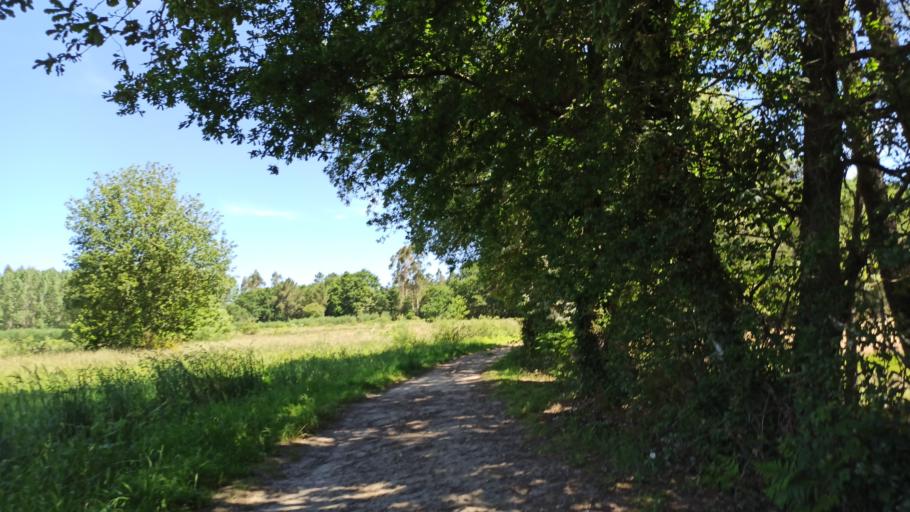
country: ES
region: Galicia
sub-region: Provincia da Coruna
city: Negreira
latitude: 42.9140
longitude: -8.7312
